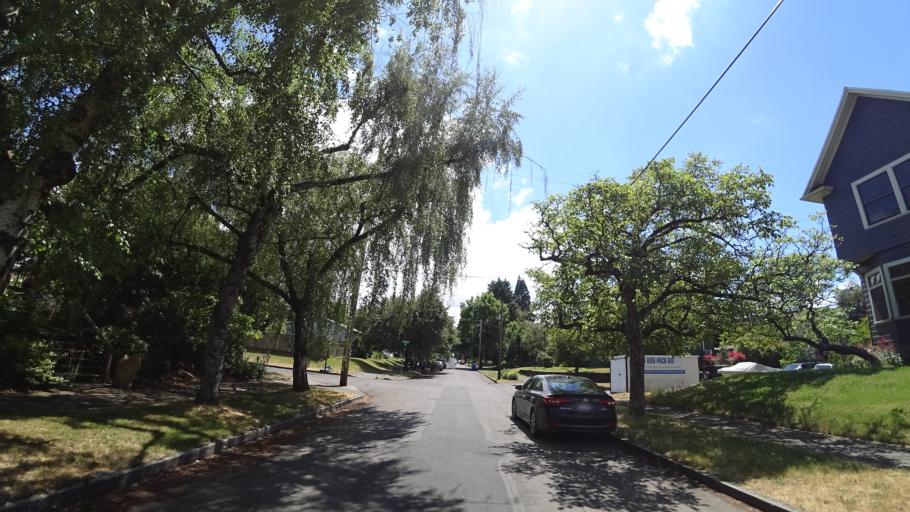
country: US
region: Oregon
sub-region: Multnomah County
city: Portland
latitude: 45.5657
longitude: -122.6802
